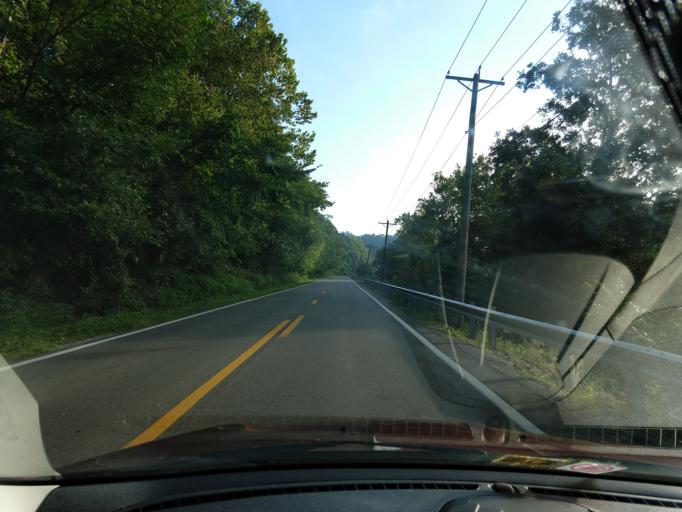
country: US
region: West Virginia
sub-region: Kanawha County
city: Charleston
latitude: 38.3828
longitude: -81.5979
